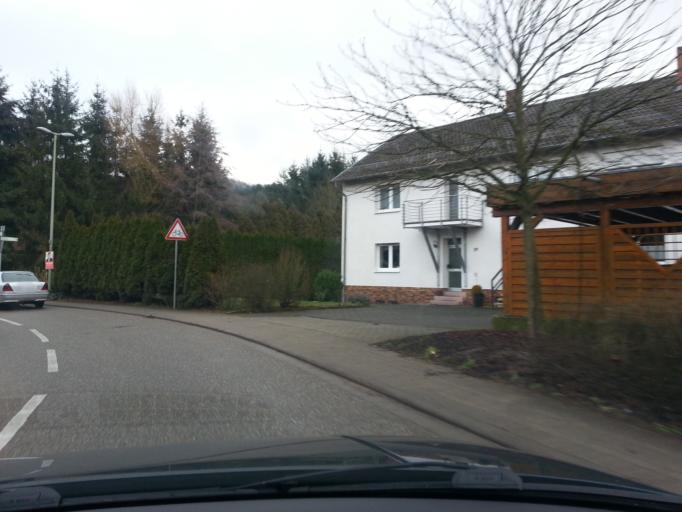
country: DE
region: Rheinland-Pfalz
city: Reichenbach-Steegen
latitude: 49.4994
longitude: 7.5436
